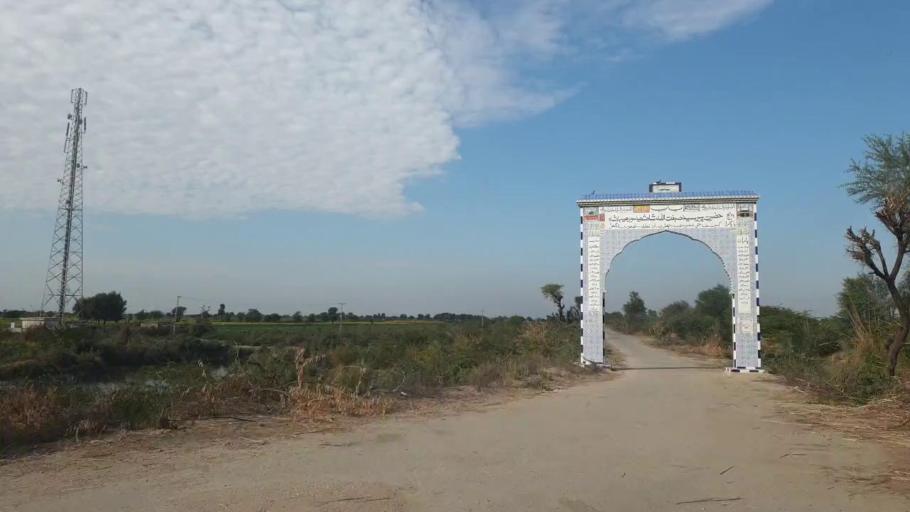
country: PK
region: Sindh
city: Sinjhoro
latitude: 26.0329
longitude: 68.8788
